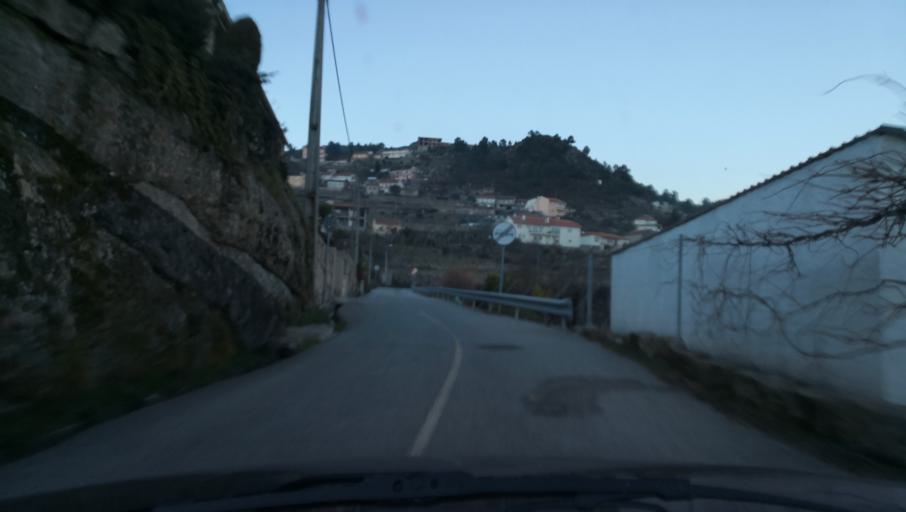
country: PT
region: Vila Real
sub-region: Vila Real
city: Vila Real
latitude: 41.3169
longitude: -7.7872
